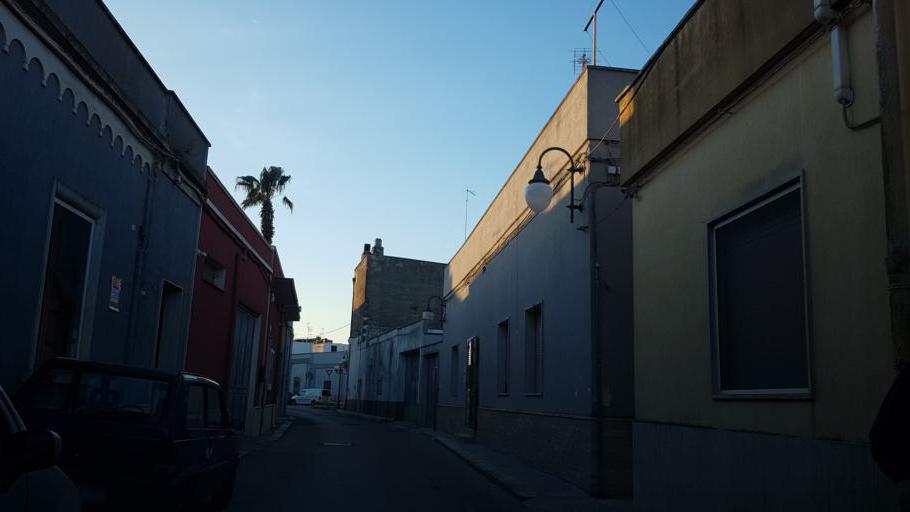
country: IT
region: Apulia
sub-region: Provincia di Brindisi
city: Tuturano
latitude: 40.5441
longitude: 17.9457
